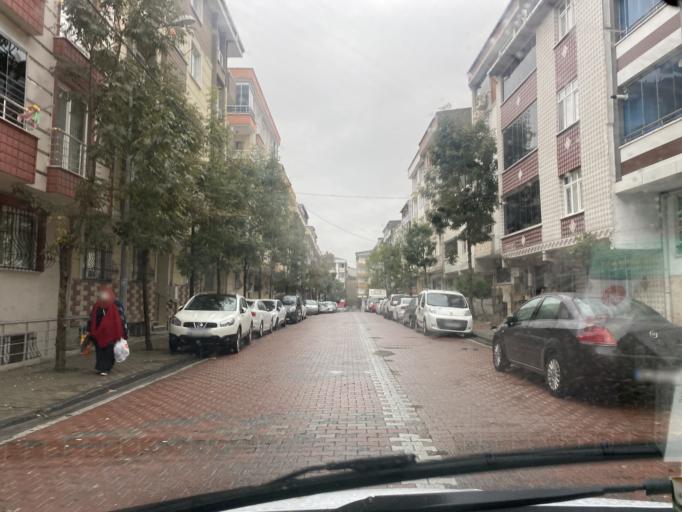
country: TR
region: Istanbul
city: Esenyurt
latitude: 41.0198
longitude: 28.6620
